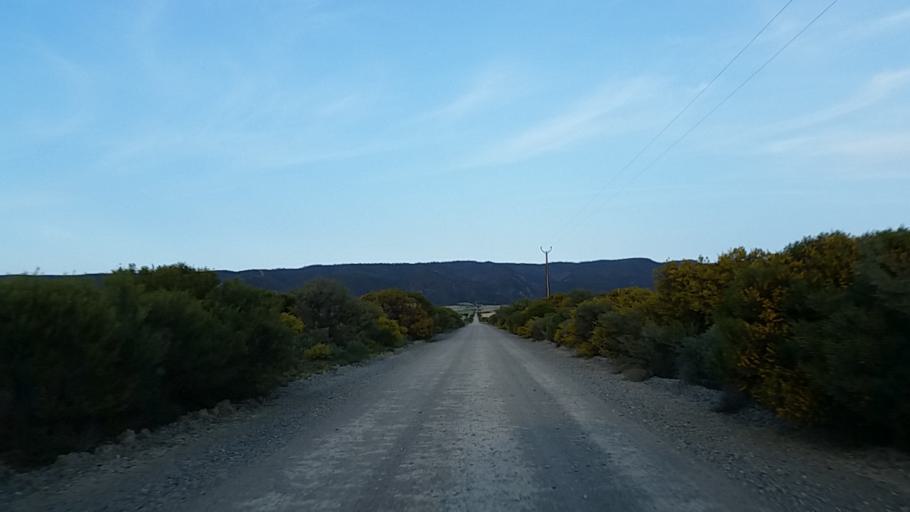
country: AU
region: South Australia
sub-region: Port Pirie City and Dists
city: Port Pirie
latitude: -33.0546
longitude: 138.0713
